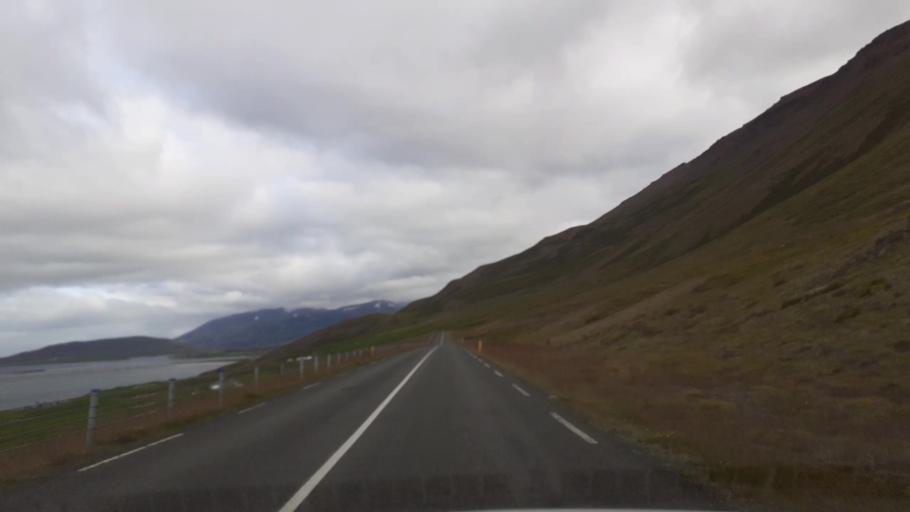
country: IS
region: Northeast
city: Akureyri
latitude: 65.8524
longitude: -18.0606
